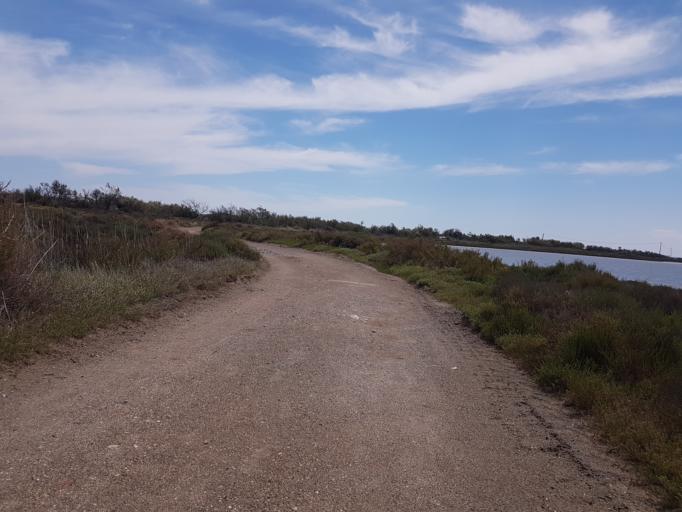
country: FR
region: Languedoc-Roussillon
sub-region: Departement de l'Herault
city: Vic-la-Gardiole
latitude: 43.4736
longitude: 3.8298
